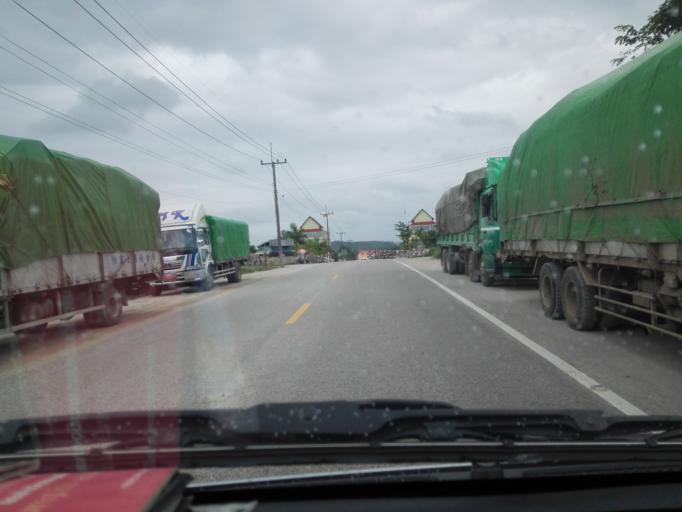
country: TH
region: Tak
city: Mae Sot
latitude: 16.6948
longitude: 98.4220
